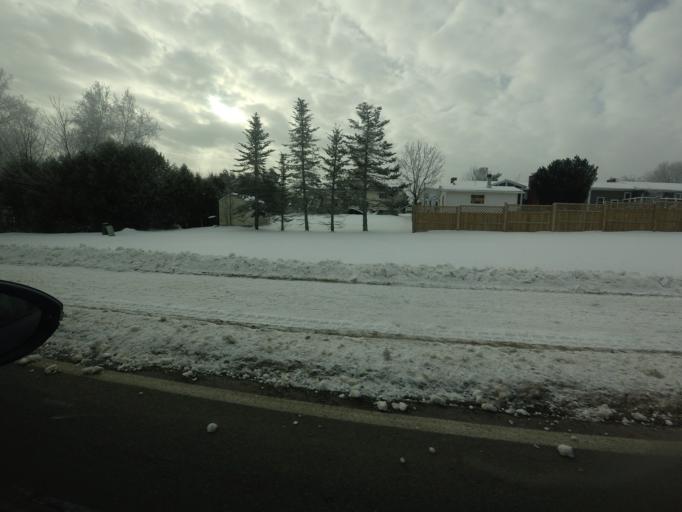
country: CA
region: New Brunswick
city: Oromocto
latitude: 45.8456
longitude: -66.5052
